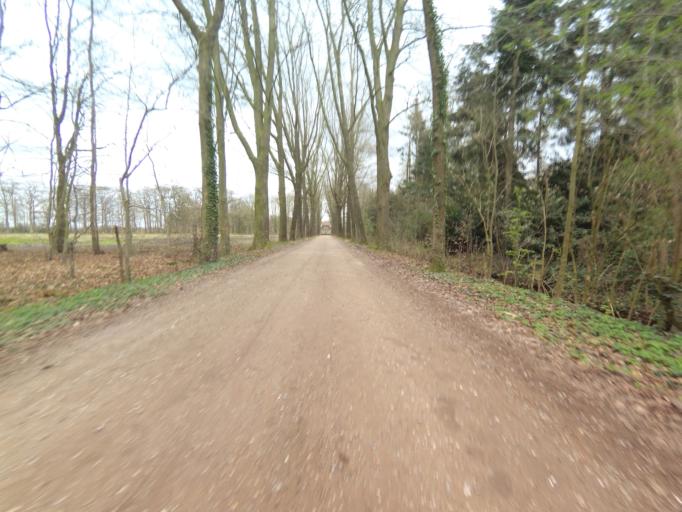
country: NL
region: Utrecht
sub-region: Gemeente Leusden
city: Leusden
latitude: 52.1561
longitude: 5.4645
